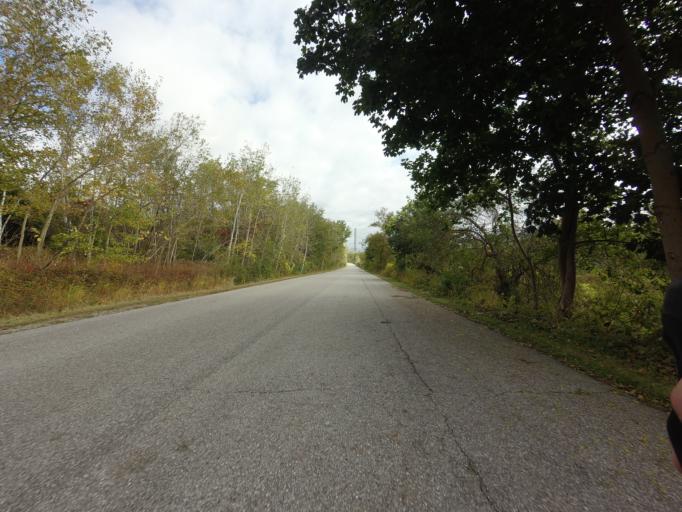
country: CA
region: Ontario
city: Scarborough
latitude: 43.7625
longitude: -79.1588
